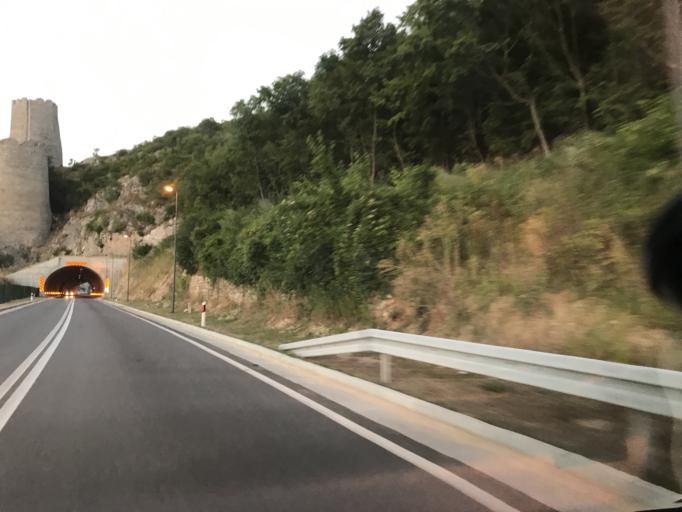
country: RO
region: Caras-Severin
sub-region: Comuna Pescari
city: Coronini
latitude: 44.6599
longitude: 21.6763
